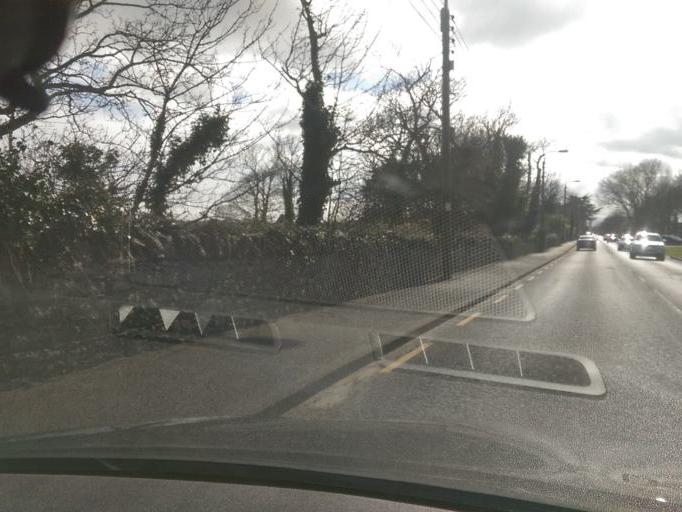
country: IE
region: Leinster
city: Portmarnock
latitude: 53.4272
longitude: -6.1299
